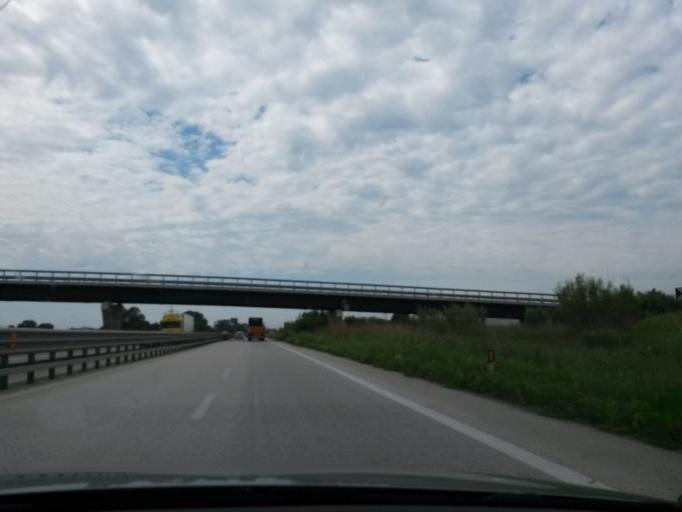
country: IT
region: Tuscany
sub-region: Provincia di Livorno
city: Piombino
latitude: 42.9798
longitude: 10.5601
